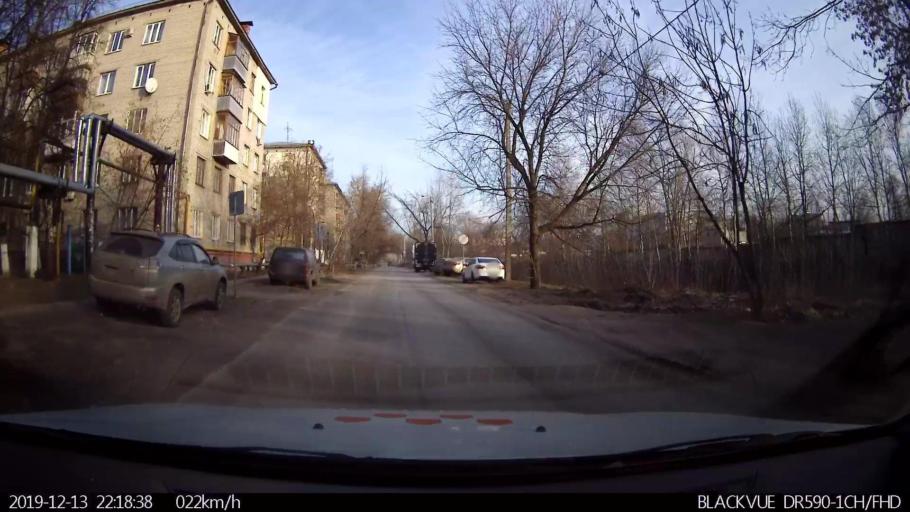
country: RU
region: Nizjnij Novgorod
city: Nizhniy Novgorod
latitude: 56.2645
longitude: 43.9158
